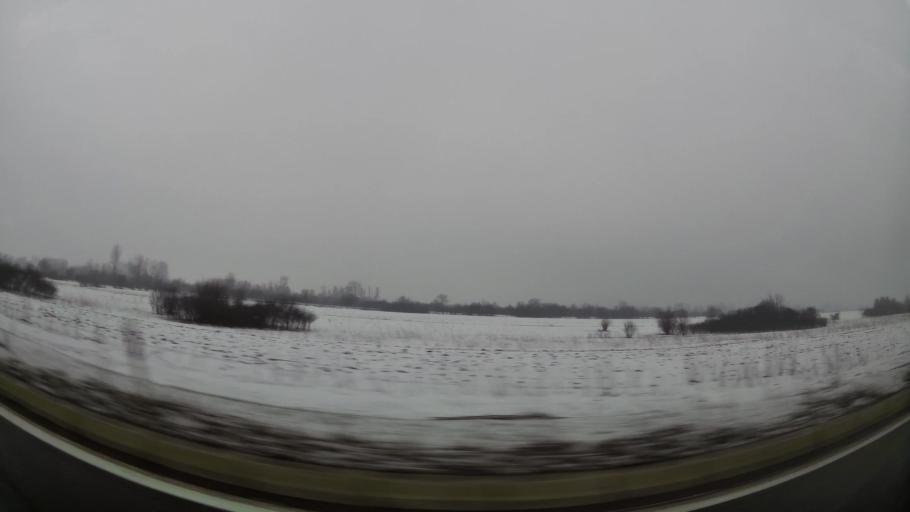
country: RS
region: Central Serbia
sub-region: Belgrade
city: Cukarica
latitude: 44.7488
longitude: 20.3736
